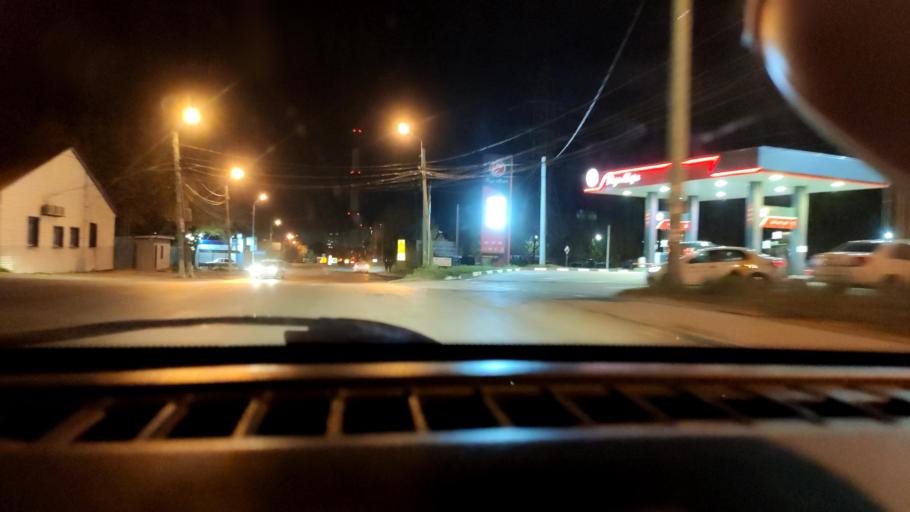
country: RU
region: Samara
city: Samara
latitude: 53.1829
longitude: 50.1634
